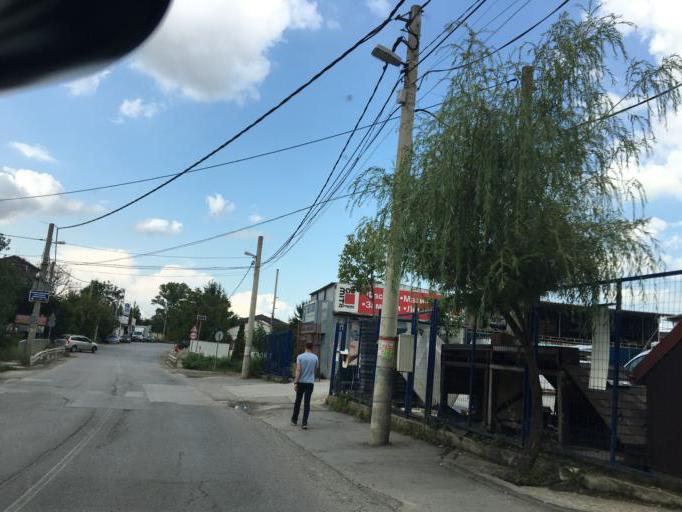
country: BG
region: Sofia-Capital
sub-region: Stolichna Obshtina
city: Sofia
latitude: 42.6401
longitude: 23.3533
